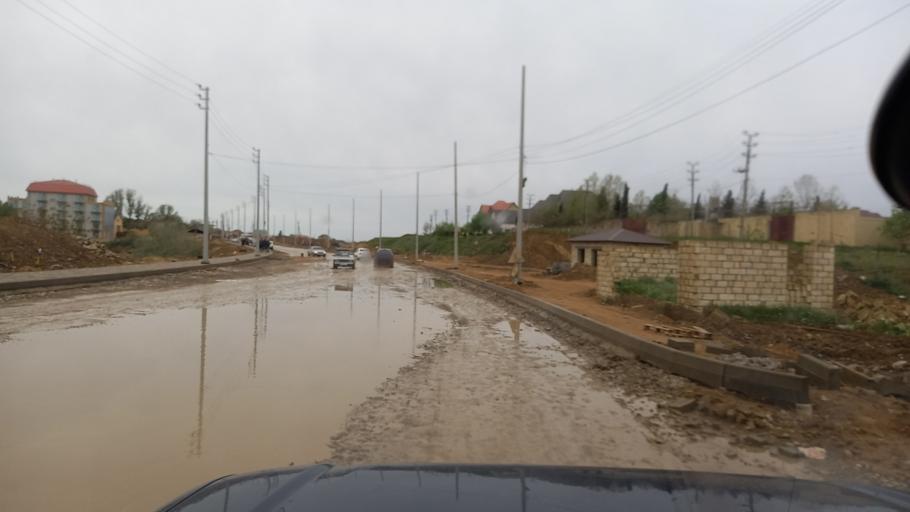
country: RU
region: Dagestan
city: Derbent
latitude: 42.0954
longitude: 48.2884
